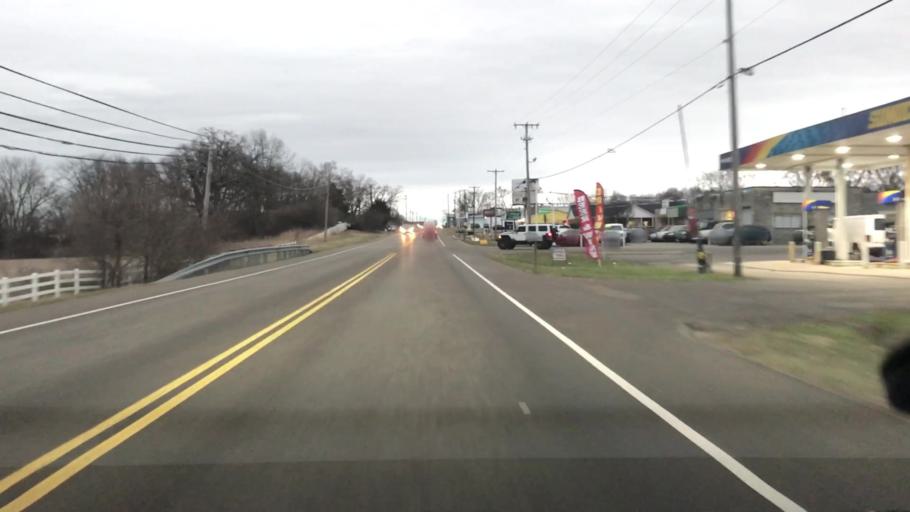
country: US
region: Ohio
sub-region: Clark County
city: Green Meadows
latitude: 39.8744
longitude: -83.9443
